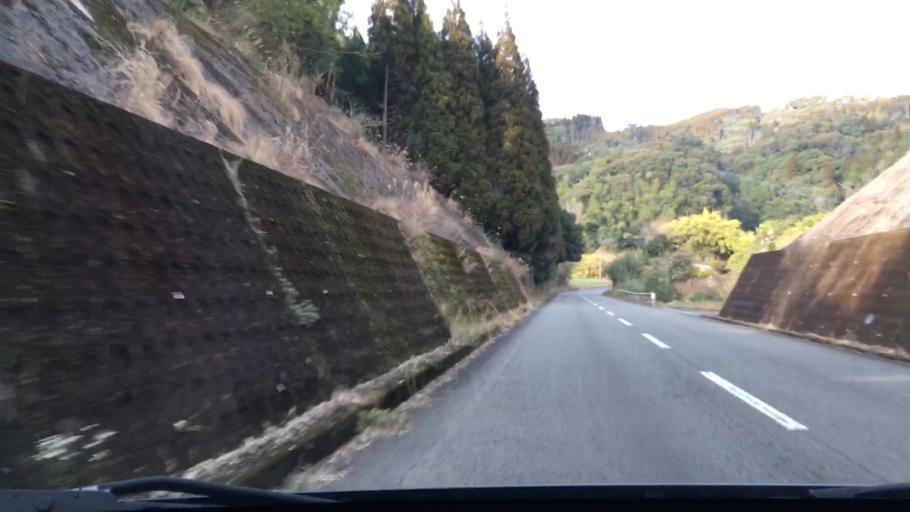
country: JP
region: Miyazaki
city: Nichinan
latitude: 31.5938
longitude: 131.3070
